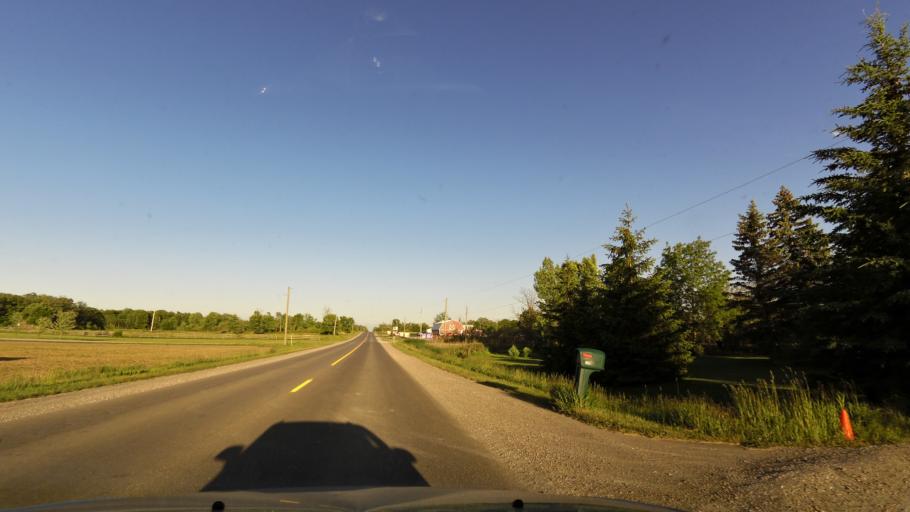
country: CA
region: Ontario
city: Ancaster
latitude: 43.0458
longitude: -80.0560
